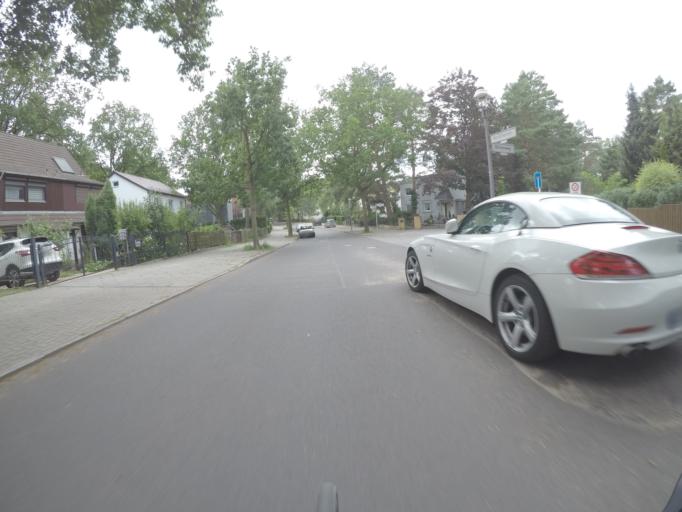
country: DE
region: Berlin
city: Frohnau
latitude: 52.6295
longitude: 13.2667
